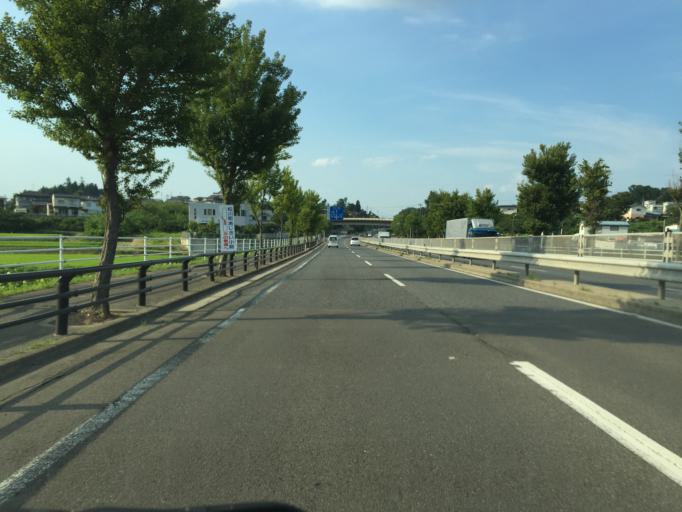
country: JP
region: Fukushima
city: Nihommatsu
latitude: 37.6489
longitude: 140.4875
